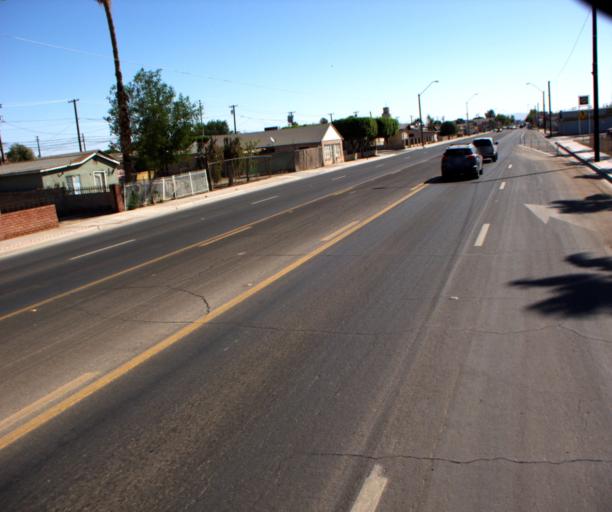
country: US
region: Arizona
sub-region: Yuma County
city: Somerton
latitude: 32.5965
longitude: -114.7172
